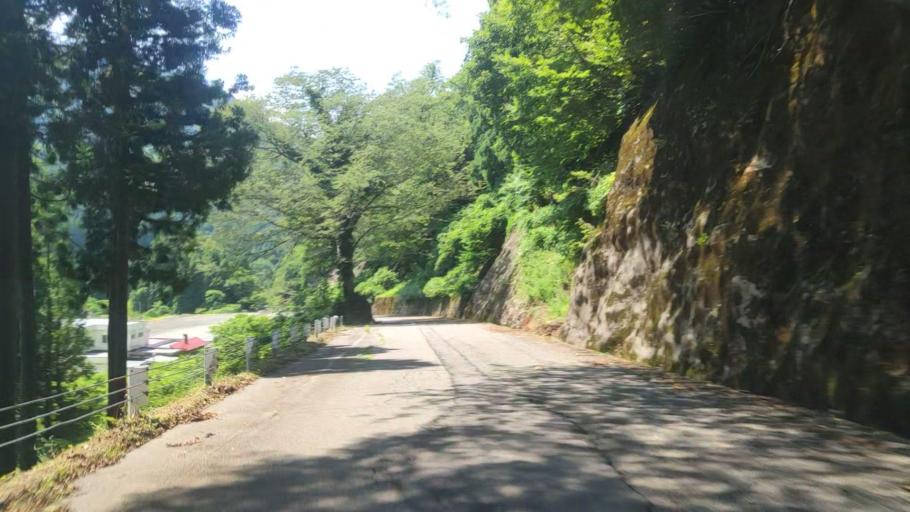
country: JP
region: Fukui
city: Katsuyama
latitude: 36.1229
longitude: 136.5073
